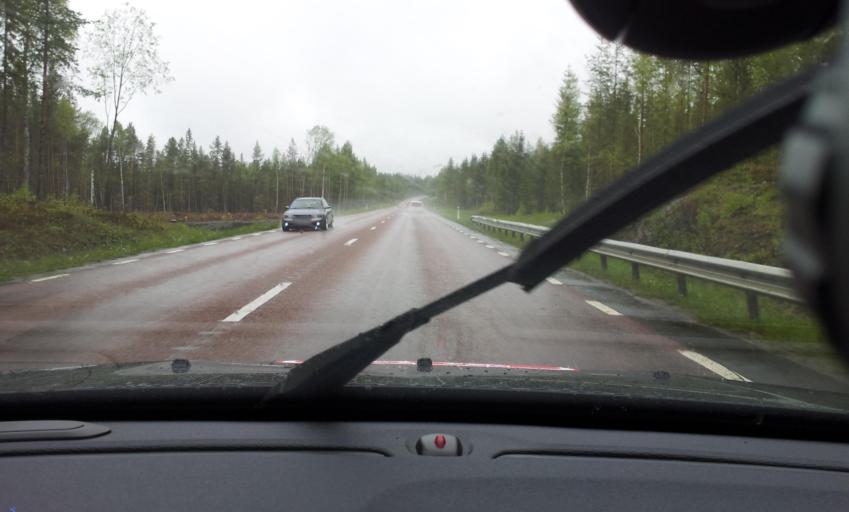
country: SE
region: Jaemtland
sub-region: Bergs Kommun
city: Hoverberg
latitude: 62.8173
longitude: 14.5169
